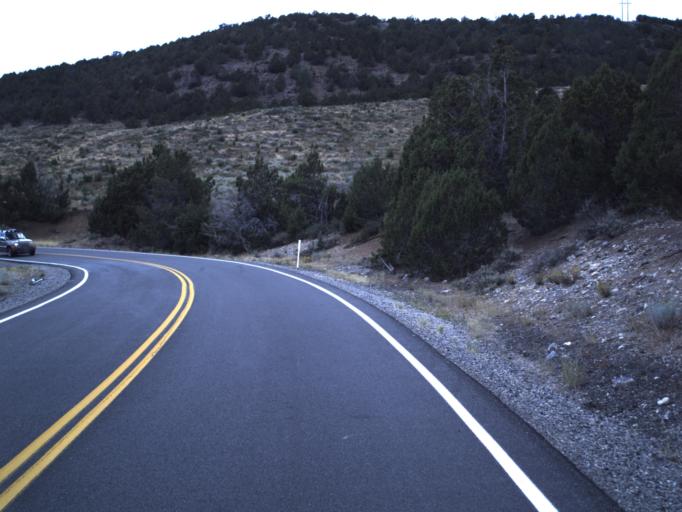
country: US
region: Utah
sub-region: Tooele County
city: Grantsville
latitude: 40.3471
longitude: -112.5648
